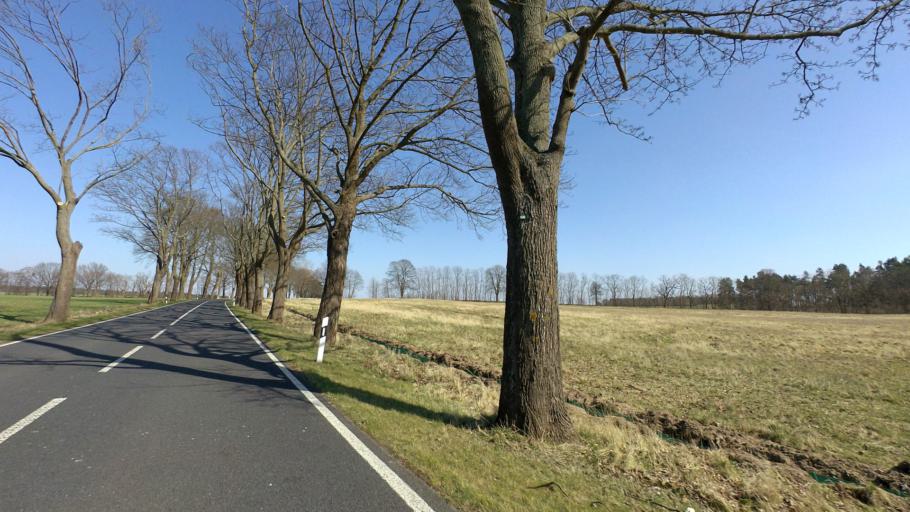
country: DE
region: Brandenburg
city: Sonnenberg
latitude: 53.0029
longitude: 13.0848
